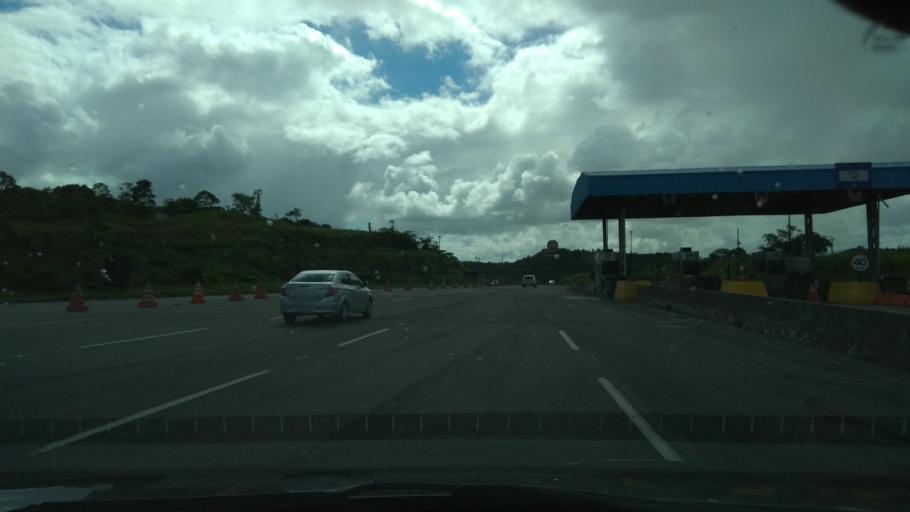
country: BR
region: Bahia
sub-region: Simoes Filho
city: Simoes Filho
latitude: -12.7498
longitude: -38.4322
